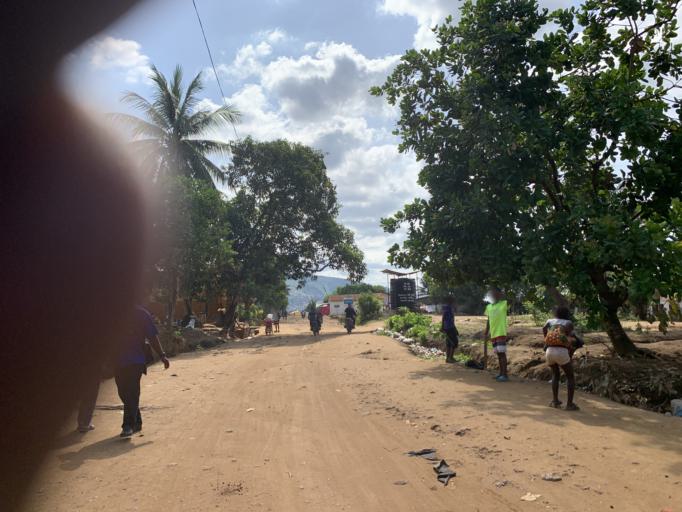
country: SL
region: Western Area
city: Waterloo
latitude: 8.3313
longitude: -13.0554
